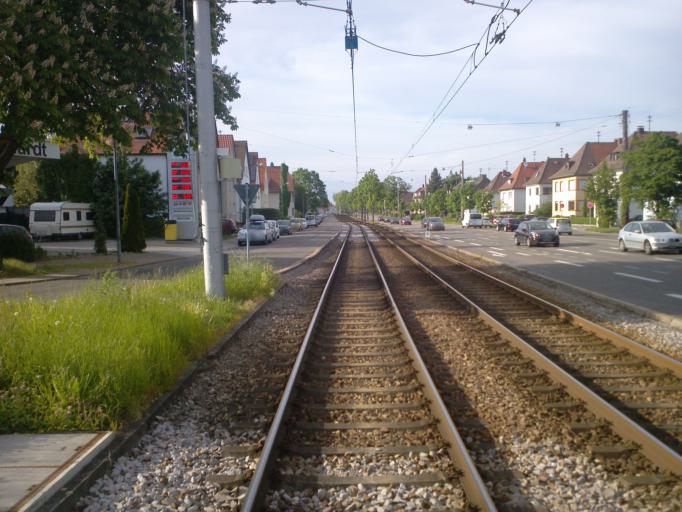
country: DE
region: Baden-Wuerttemberg
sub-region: Karlsruhe Region
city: Ettlingen
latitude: 48.9664
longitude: 8.4047
